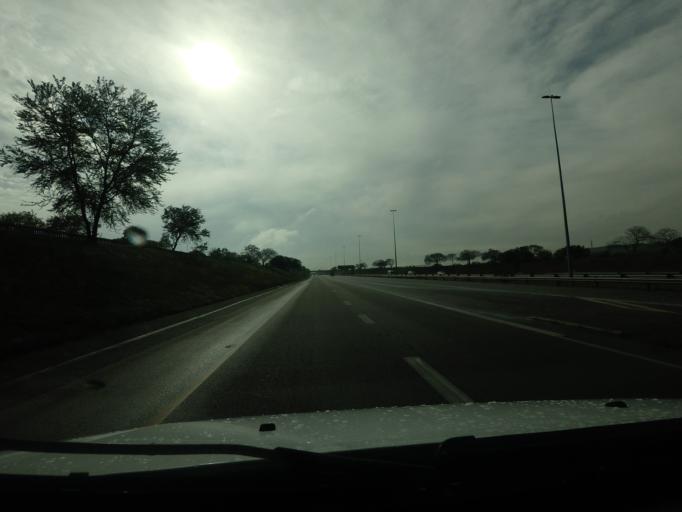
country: ZA
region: Gauteng
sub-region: City of Tshwane Metropolitan Municipality
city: Pretoria
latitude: -25.7400
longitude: 28.2703
